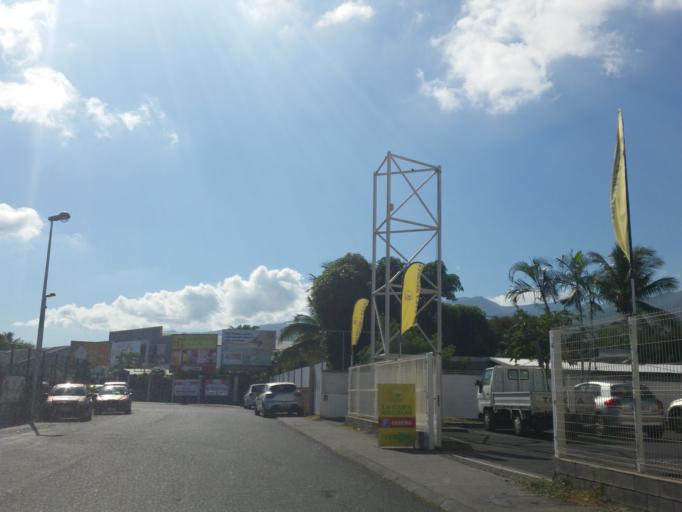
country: RE
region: Reunion
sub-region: Reunion
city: Saint-Paul
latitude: -20.9844
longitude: 55.2931
